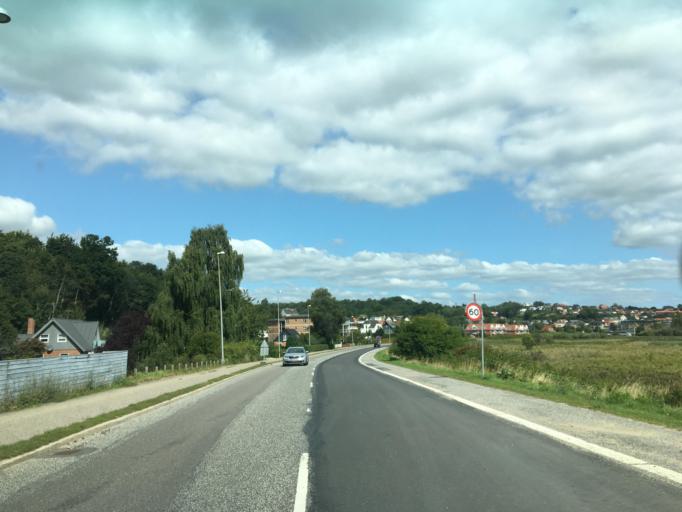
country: DK
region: North Denmark
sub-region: Mariagerfjord Kommune
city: Hobro
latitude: 56.6387
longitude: 9.7805
